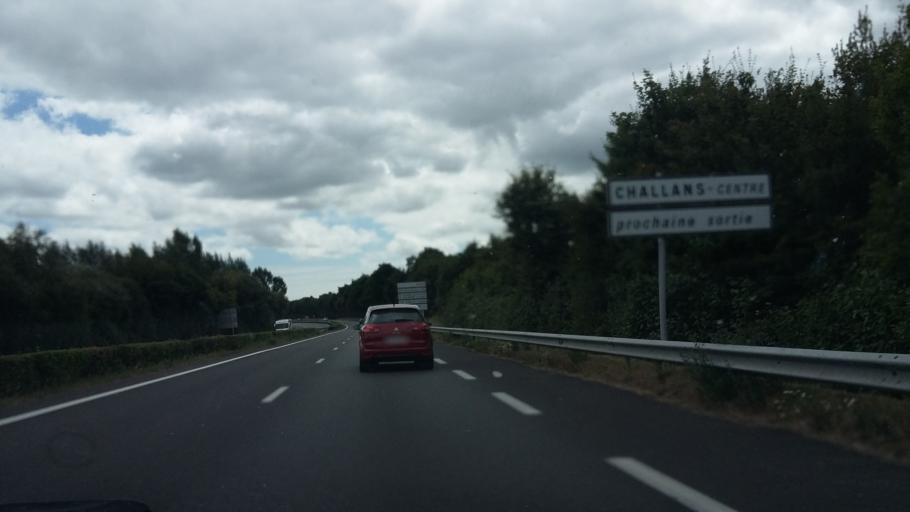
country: FR
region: Pays de la Loire
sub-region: Departement de la Vendee
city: Challans
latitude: 46.8464
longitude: -1.8520
